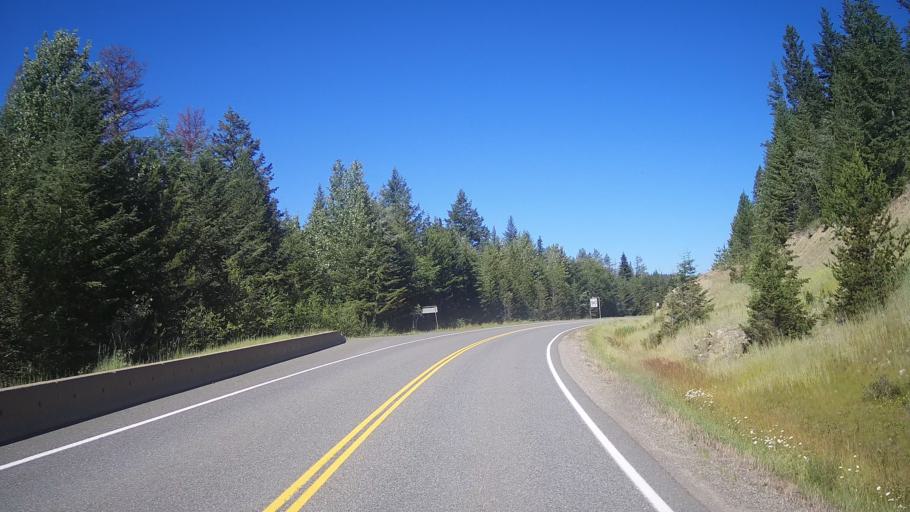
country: CA
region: British Columbia
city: Kamloops
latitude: 51.4724
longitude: -120.5507
